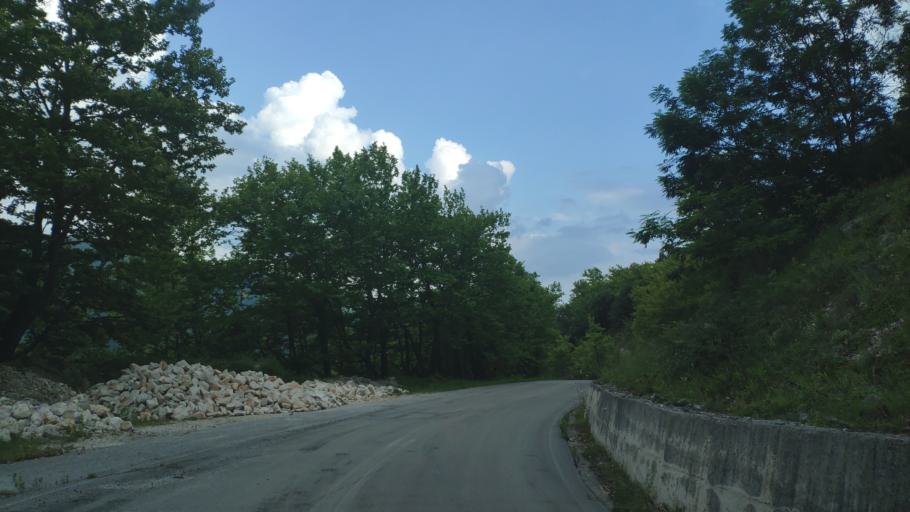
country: GR
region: Epirus
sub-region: Nomos Artas
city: Agios Dimitrios
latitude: 39.4376
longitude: 21.0135
